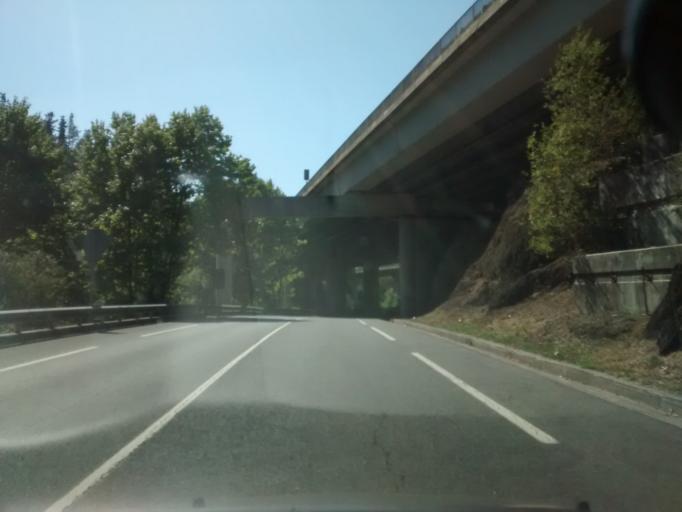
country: ES
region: Basque Country
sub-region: Provincia de Guipuzcoa
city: Eibar
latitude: 43.1923
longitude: -2.4397
